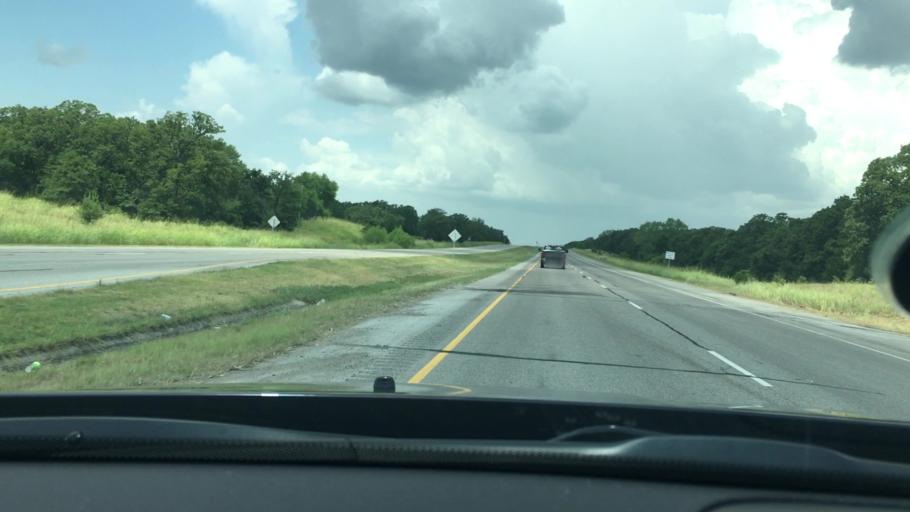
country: US
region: Oklahoma
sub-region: Carter County
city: Ardmore
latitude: 34.1361
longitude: -97.1105
